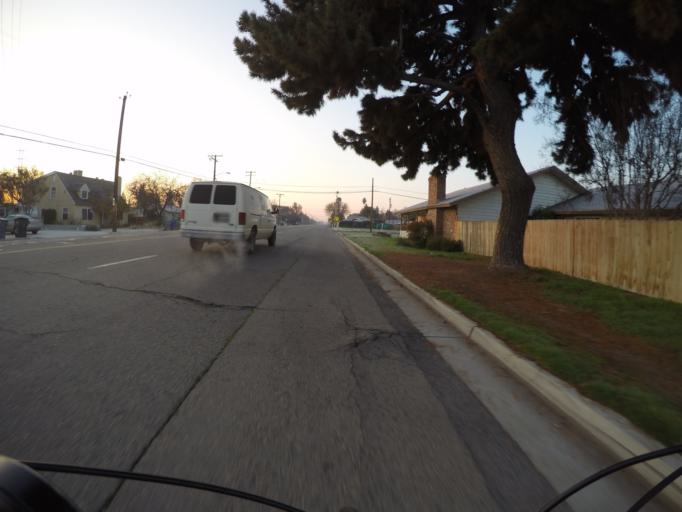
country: US
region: California
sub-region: Fresno County
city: Fresno
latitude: 36.7705
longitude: -119.7455
